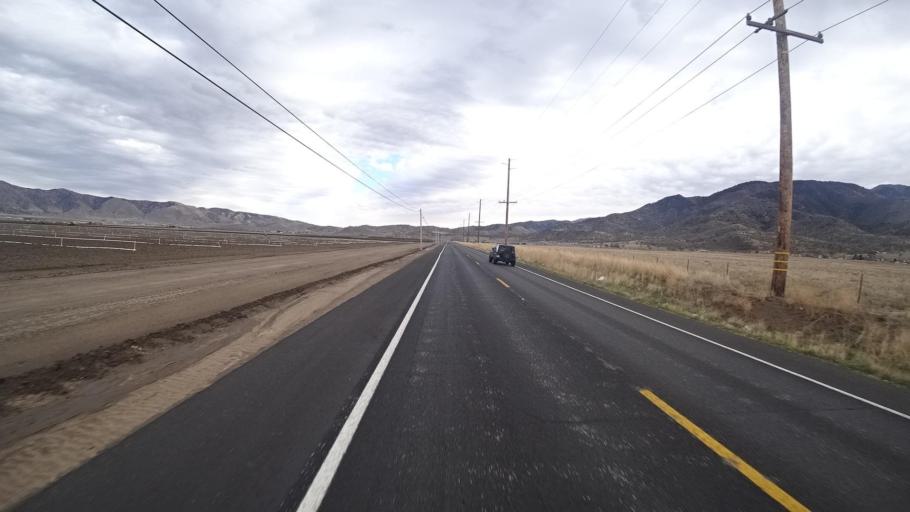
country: US
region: California
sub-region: Kern County
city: Stallion Springs
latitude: 35.0946
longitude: -118.6219
